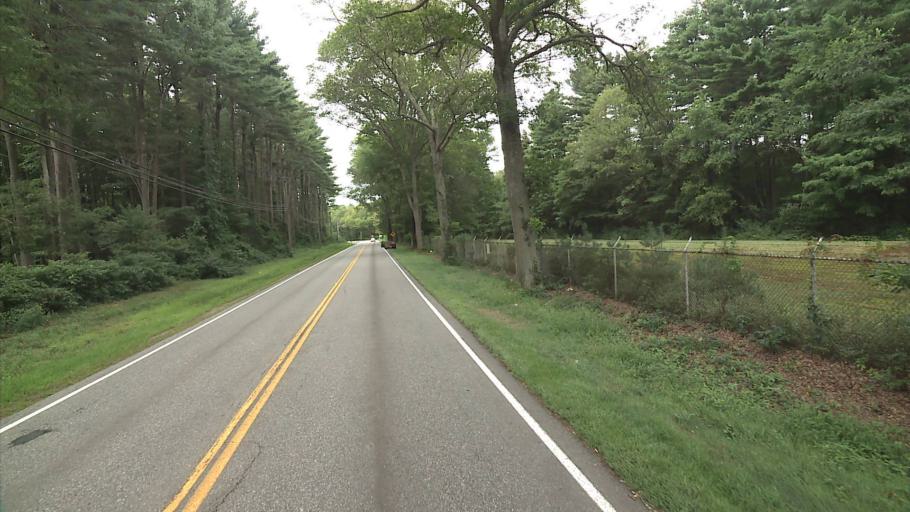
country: US
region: Connecticut
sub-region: New London County
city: Oxoboxo River
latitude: 41.4079
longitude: -72.1833
